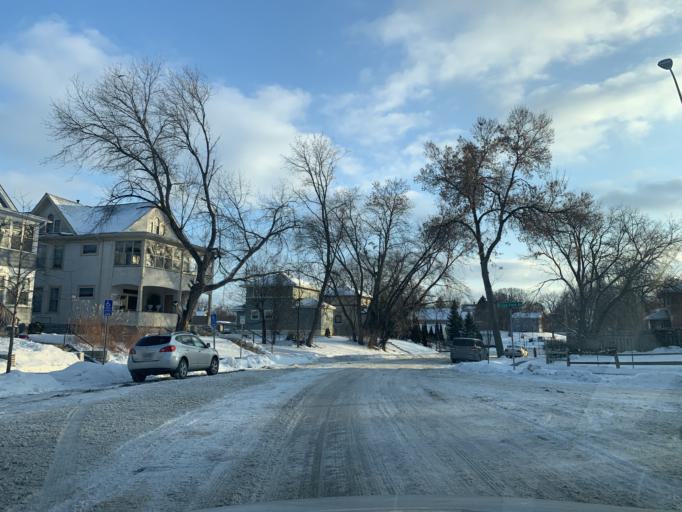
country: US
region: Minnesota
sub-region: Hennepin County
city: Minneapolis
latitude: 44.9876
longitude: -93.2997
